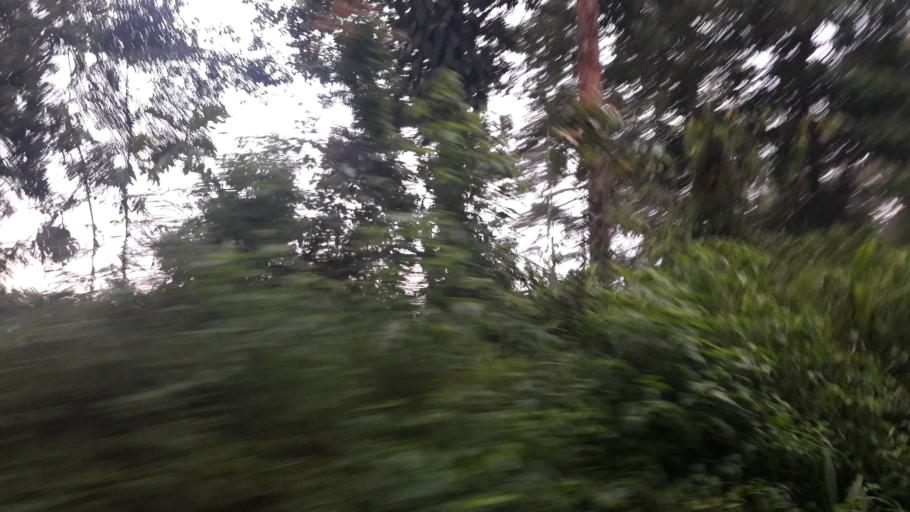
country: ID
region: West Java
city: Cipeundeuy
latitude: -6.6697
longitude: 106.5156
